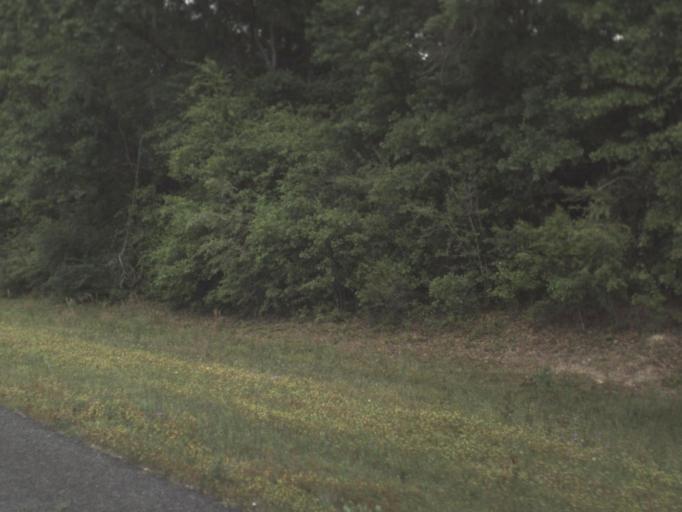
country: US
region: Florida
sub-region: Escambia County
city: Molino
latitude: 30.7454
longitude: -87.3480
